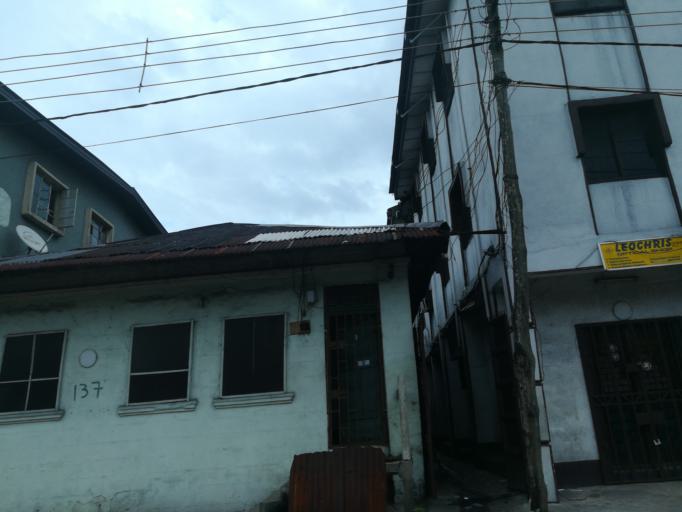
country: NG
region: Rivers
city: Port Harcourt
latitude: 4.7607
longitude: 7.0274
